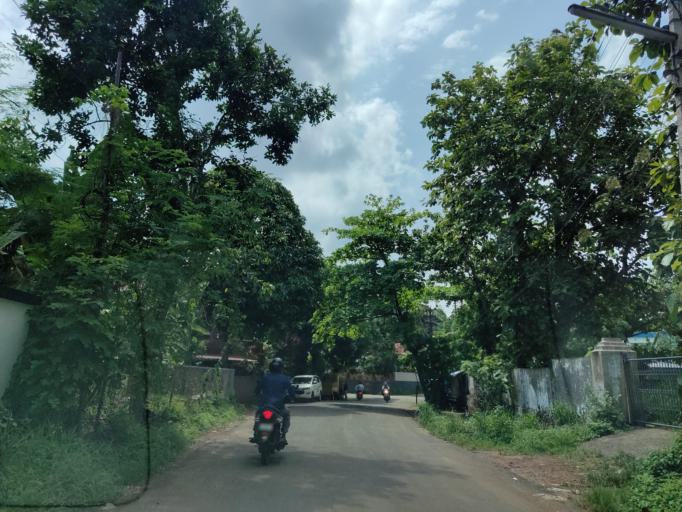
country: IN
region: Kerala
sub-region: Alappuzha
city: Mavelikara
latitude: 9.2549
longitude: 76.5668
